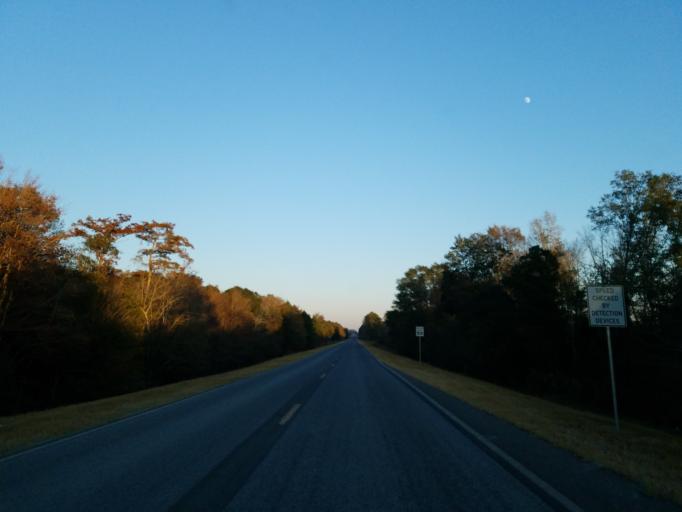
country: US
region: Georgia
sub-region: Turner County
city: Ashburn
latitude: 31.7210
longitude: -83.4548
